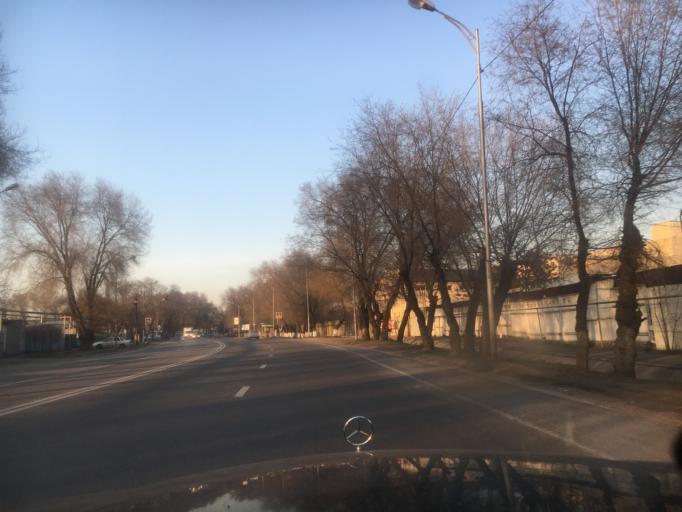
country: KZ
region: Almaty Oblysy
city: Pervomayskiy
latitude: 43.3601
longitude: 76.9810
